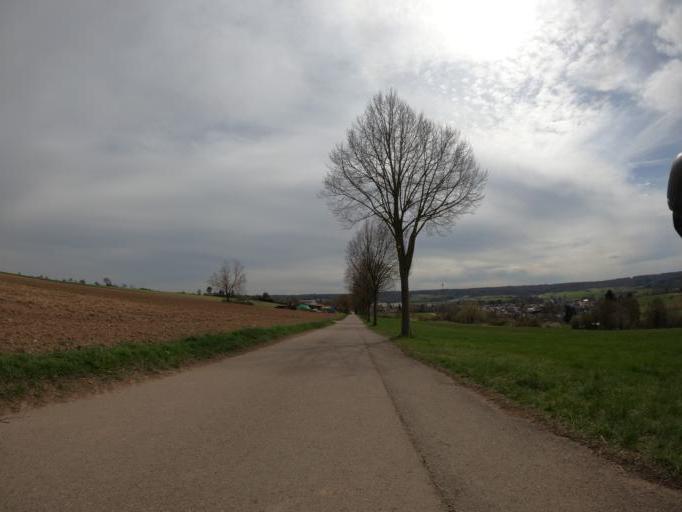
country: DE
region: Baden-Wuerttemberg
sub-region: Regierungsbezirk Stuttgart
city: Waldenbuch
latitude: 48.6492
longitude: 9.1356
